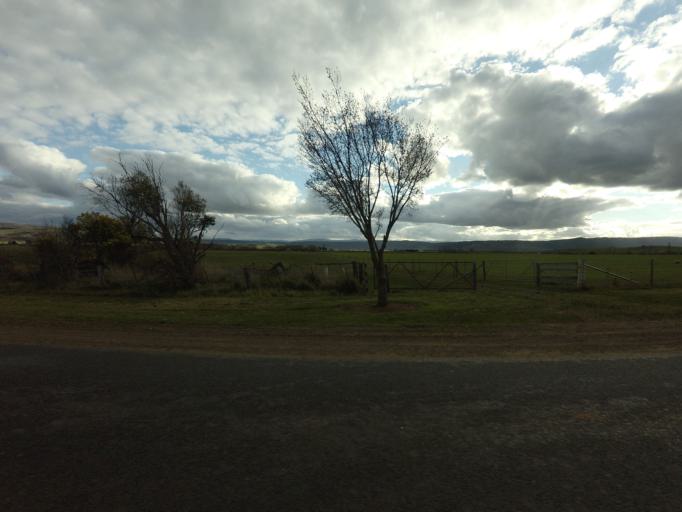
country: AU
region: Tasmania
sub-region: Northern Midlands
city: Evandale
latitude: -42.0188
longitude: 147.4919
